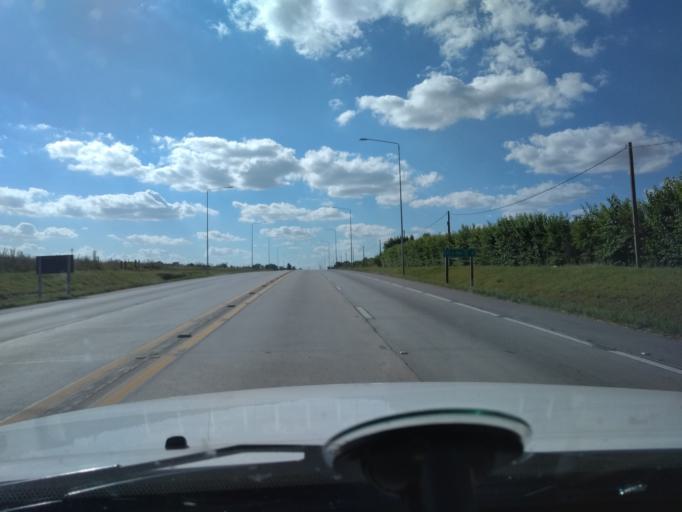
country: UY
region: Canelones
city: La Paz
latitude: -34.7899
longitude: -56.2135
